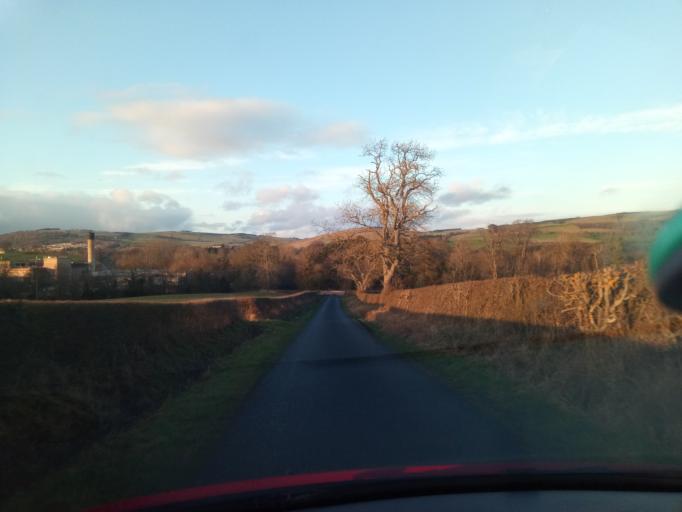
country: GB
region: Scotland
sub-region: The Scottish Borders
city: Melrose
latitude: 55.5936
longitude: -2.7372
